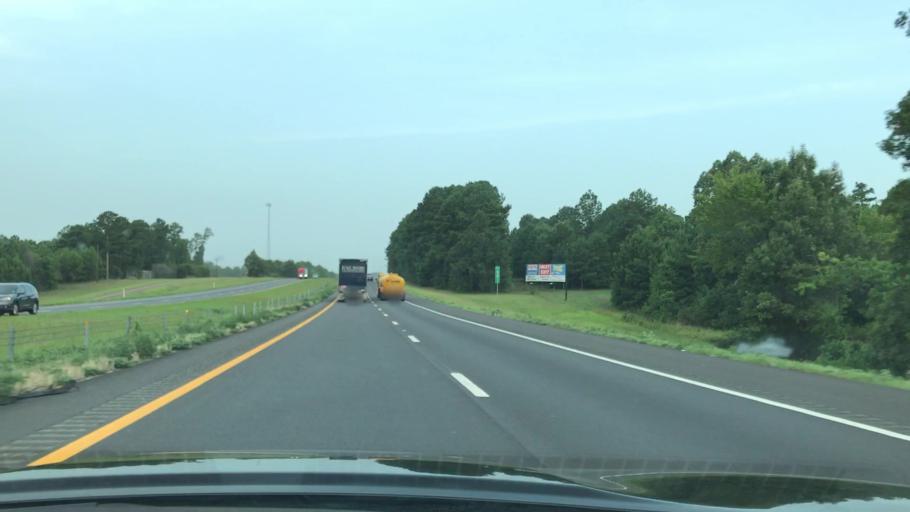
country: US
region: Texas
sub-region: Harrison County
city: Hallsville
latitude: 32.4651
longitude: -94.6336
